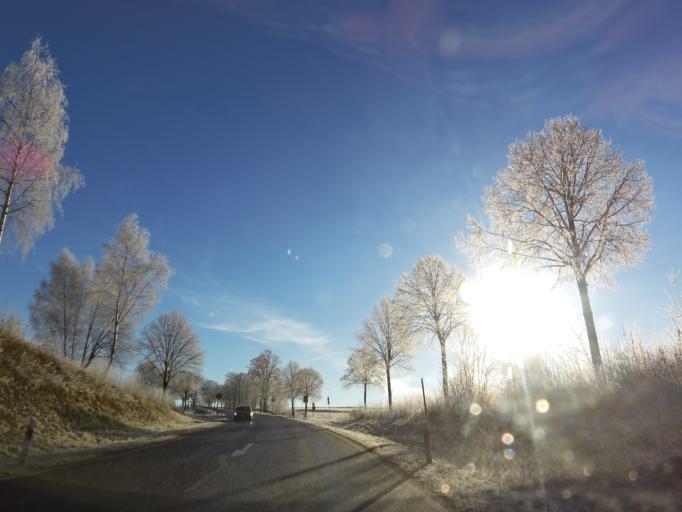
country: DE
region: Bavaria
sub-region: Upper Franconia
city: Wunsiedel
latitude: 50.0296
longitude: 12.0074
